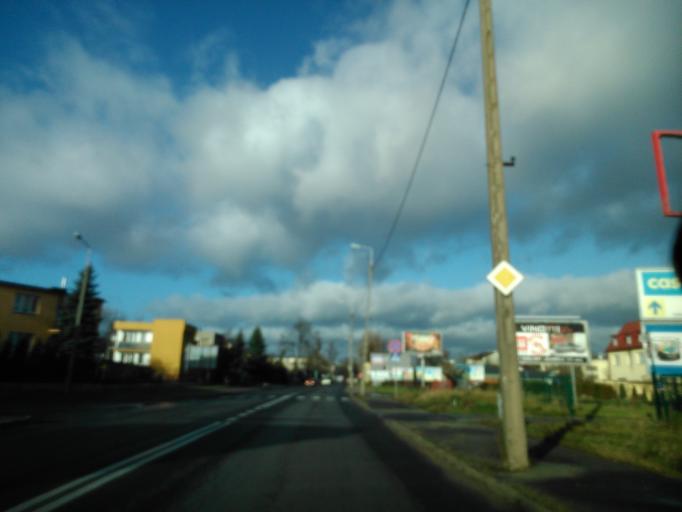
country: PL
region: Kujawsko-Pomorskie
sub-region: Torun
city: Torun
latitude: 52.9968
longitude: 18.6244
